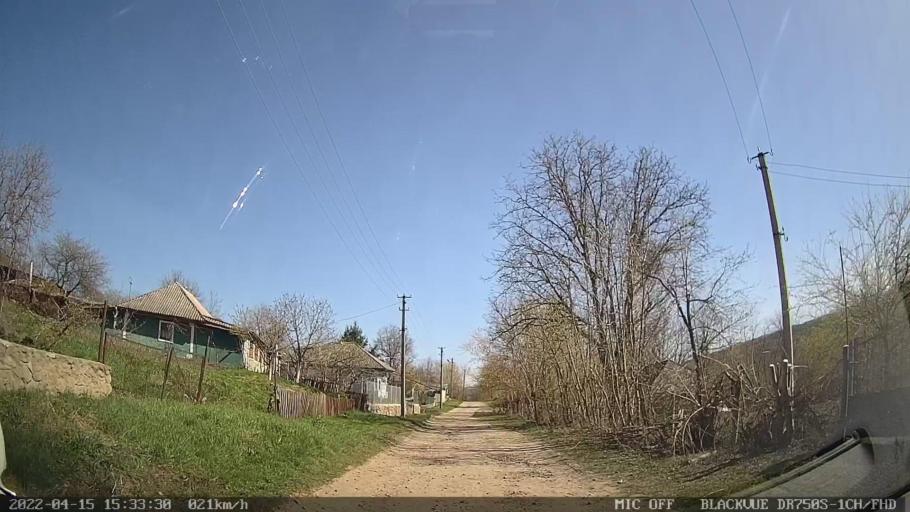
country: MD
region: Raionul Ocnita
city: Otaci
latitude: 48.3495
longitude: 27.9238
